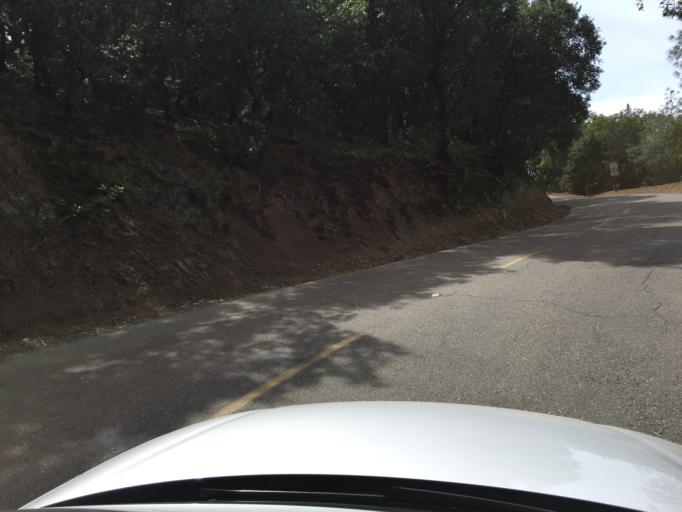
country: US
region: California
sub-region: Contra Costa County
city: Diablo
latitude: 37.8643
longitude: -121.9301
